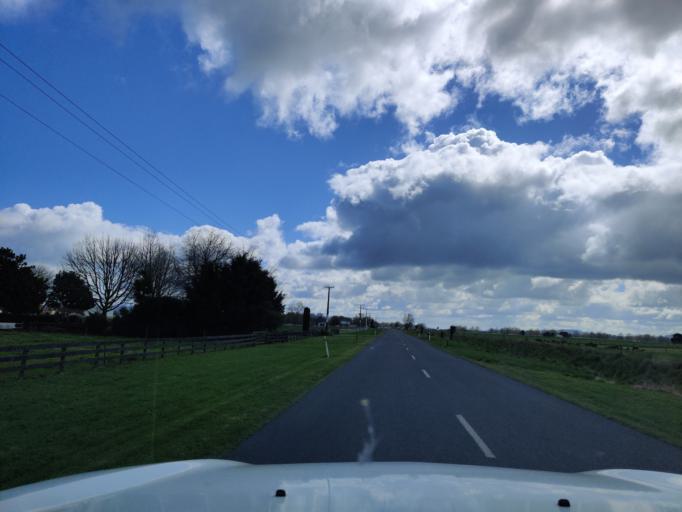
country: NZ
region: Waikato
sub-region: Hamilton City
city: Hamilton
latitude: -37.6232
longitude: 175.3213
